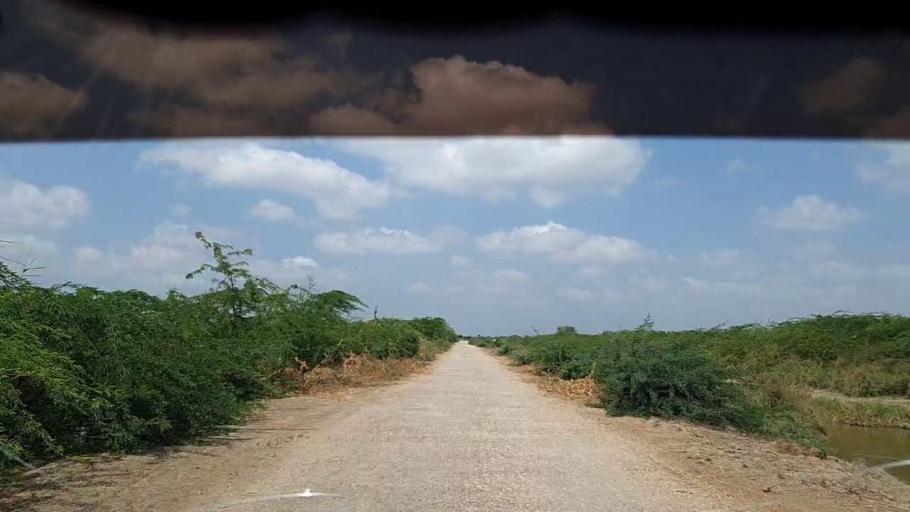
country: PK
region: Sindh
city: Kadhan
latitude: 24.5853
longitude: 68.9699
